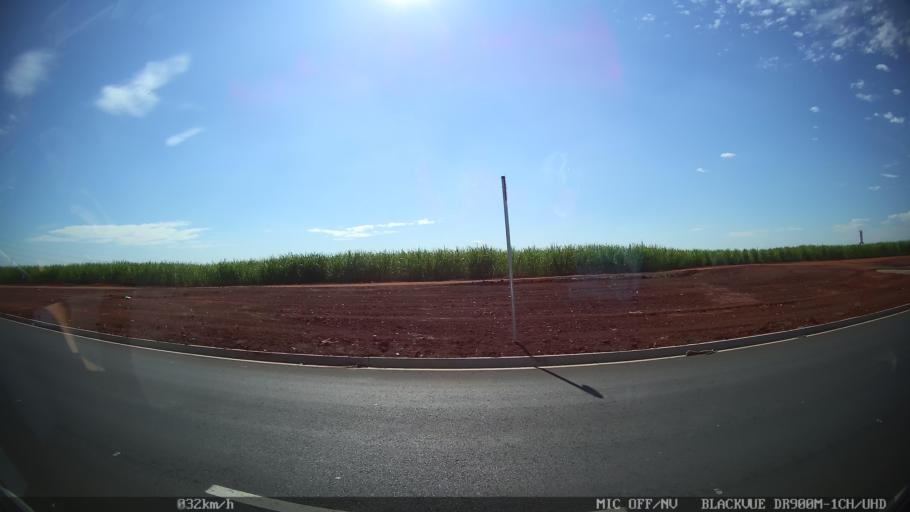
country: BR
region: Sao Paulo
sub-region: Santa Barbara D'Oeste
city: Santa Barbara d'Oeste
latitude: -22.7252
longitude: -47.4083
